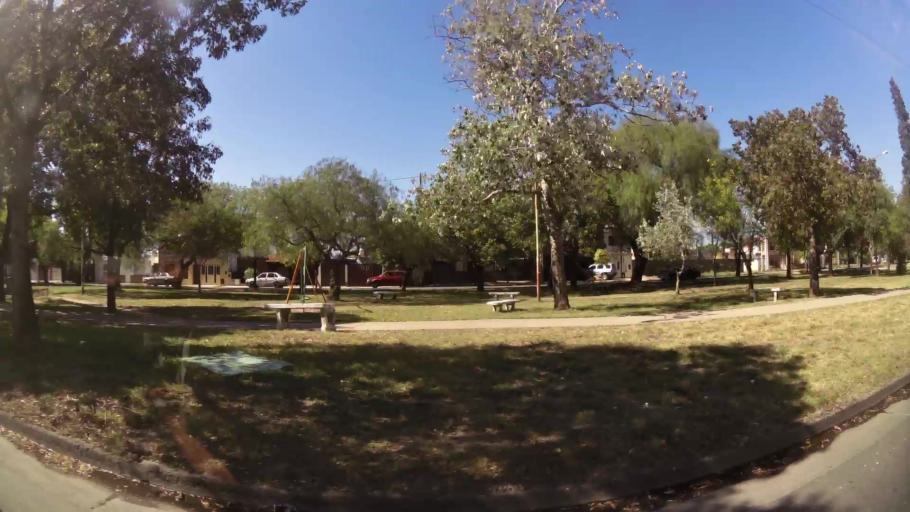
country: AR
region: Cordoba
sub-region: Departamento de Capital
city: Cordoba
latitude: -31.4354
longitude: -64.1400
